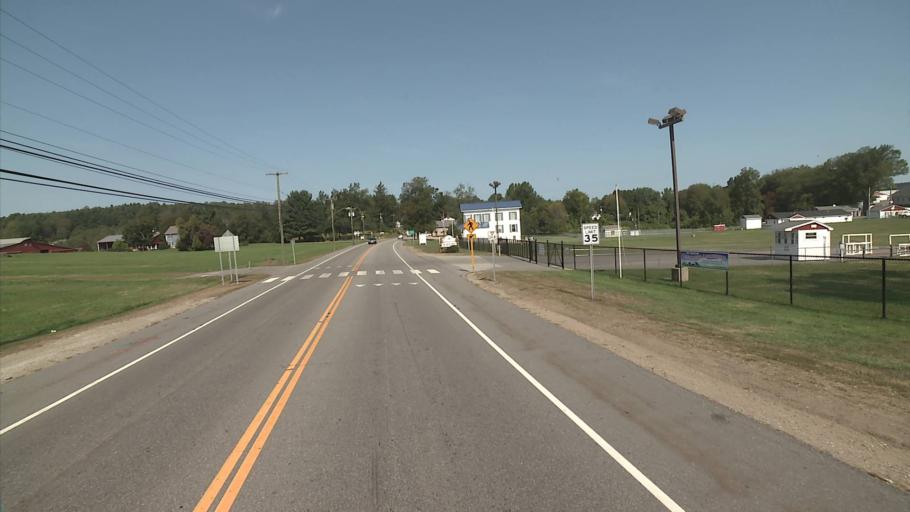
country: US
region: Connecticut
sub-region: Windham County
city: South Woodstock
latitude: 41.9349
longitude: -71.9574
